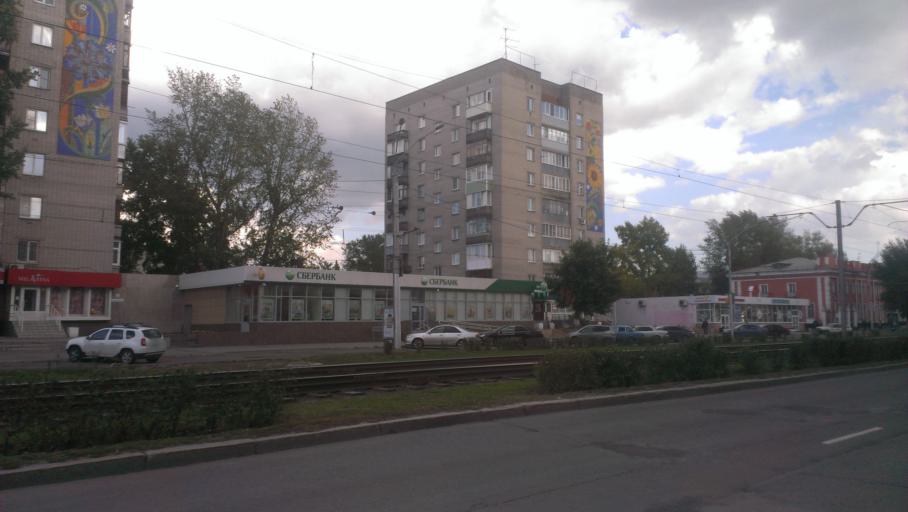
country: RU
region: Altai Krai
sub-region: Gorod Barnaulskiy
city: Barnaul
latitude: 53.3597
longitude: 83.7643
